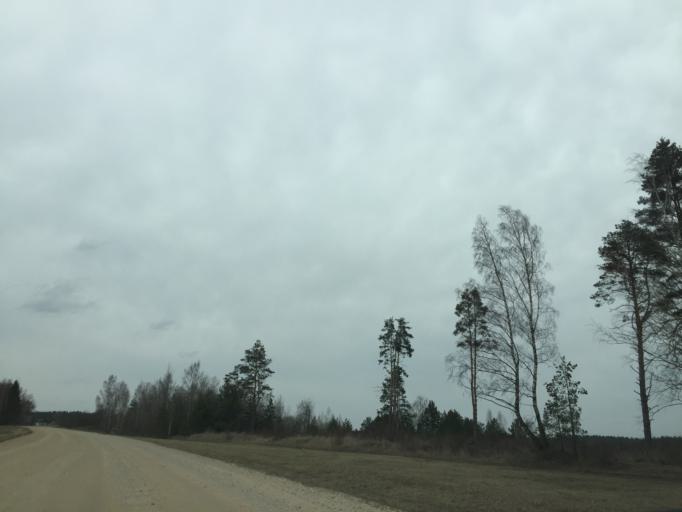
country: LV
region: Livani
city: Livani
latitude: 56.3042
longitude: 26.1702
